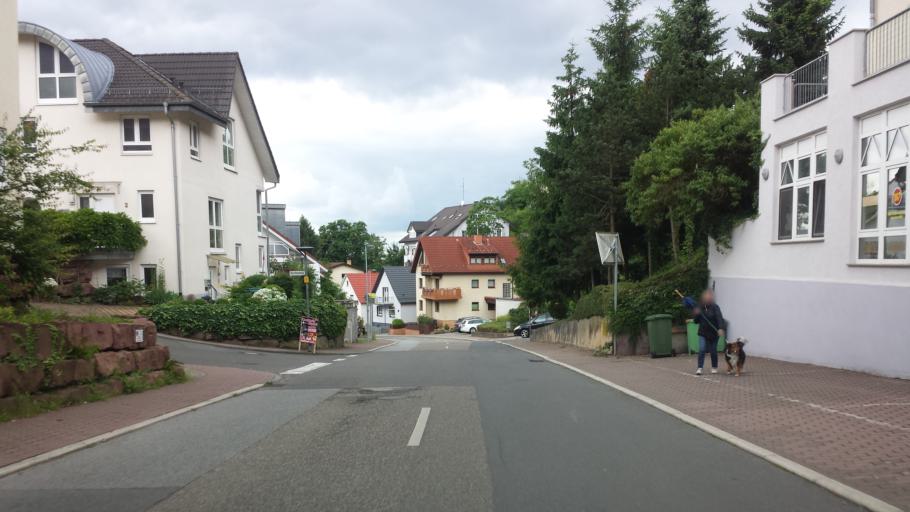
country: DE
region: Baden-Wuerttemberg
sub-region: Karlsruhe Region
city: Nussloch
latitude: 49.3222
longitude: 8.7049
